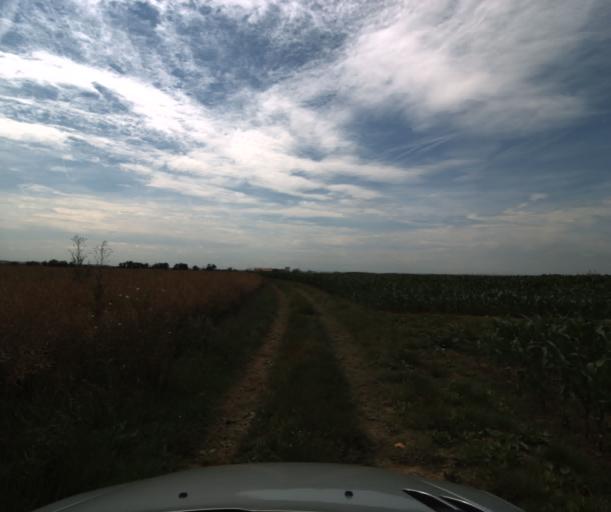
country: FR
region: Midi-Pyrenees
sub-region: Departement de la Haute-Garonne
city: Lacasse
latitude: 43.4171
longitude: 1.2627
